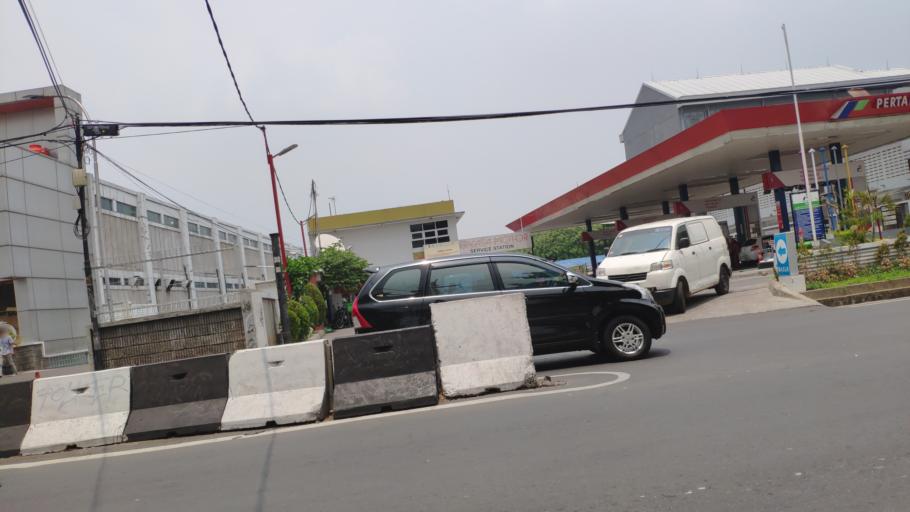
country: ID
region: Banten
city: South Tangerang
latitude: -6.2704
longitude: 106.7654
